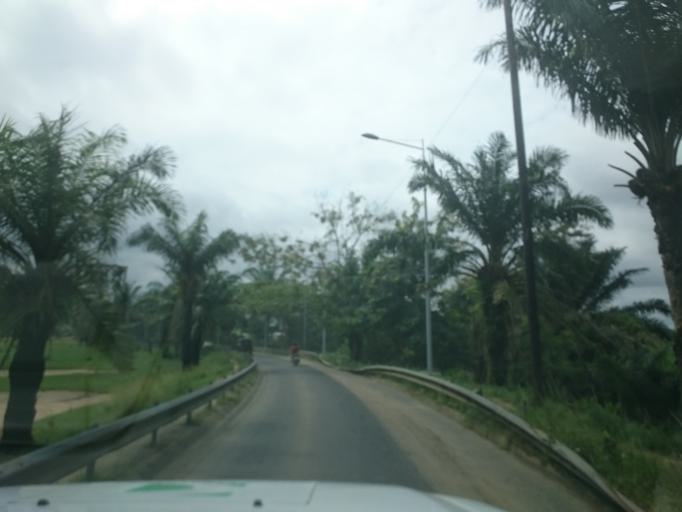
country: CM
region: Littoral
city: Douala
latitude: 4.0159
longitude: 9.6992
